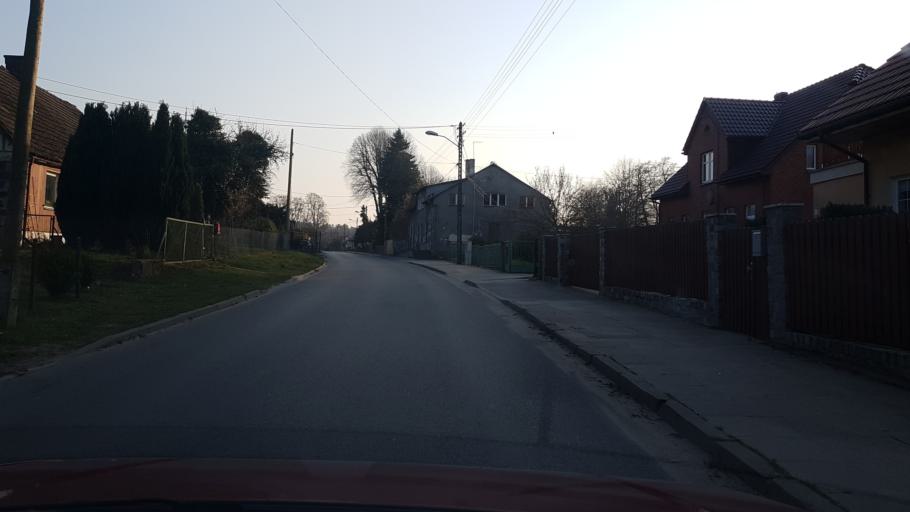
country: PL
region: West Pomeranian Voivodeship
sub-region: Powiat gryfinski
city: Stare Czarnowo
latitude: 53.3423
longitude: 14.7517
